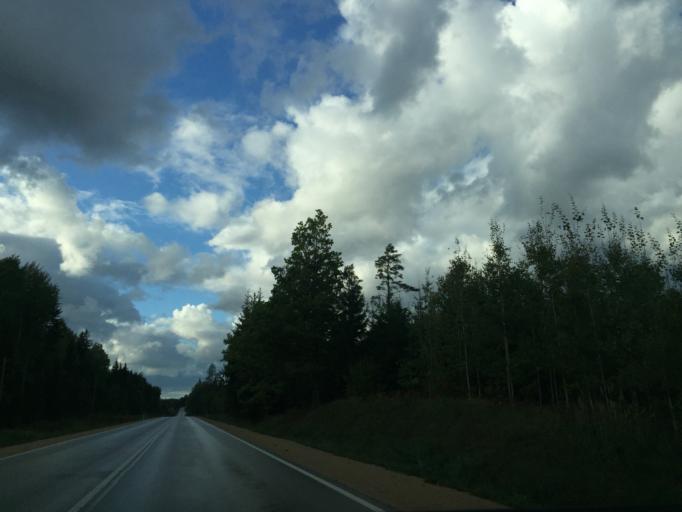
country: LV
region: Ligatne
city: Ligatne
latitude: 57.1563
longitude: 25.0653
